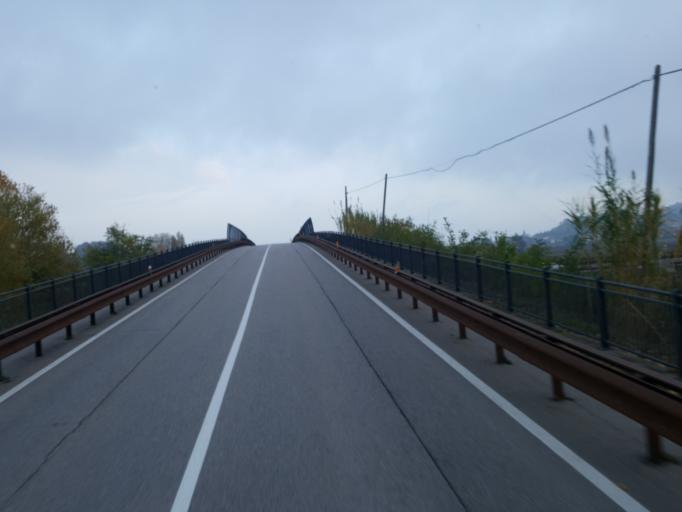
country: IT
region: Veneto
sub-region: Provincia di Verona
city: Pastrengo
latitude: 45.5093
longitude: 10.7828
